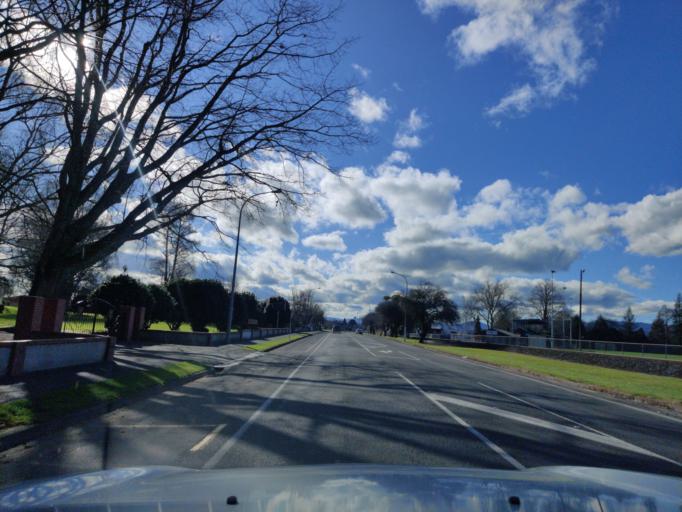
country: NZ
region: Waikato
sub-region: Matamata-Piako District
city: Matamata
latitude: -37.8170
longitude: 175.7711
